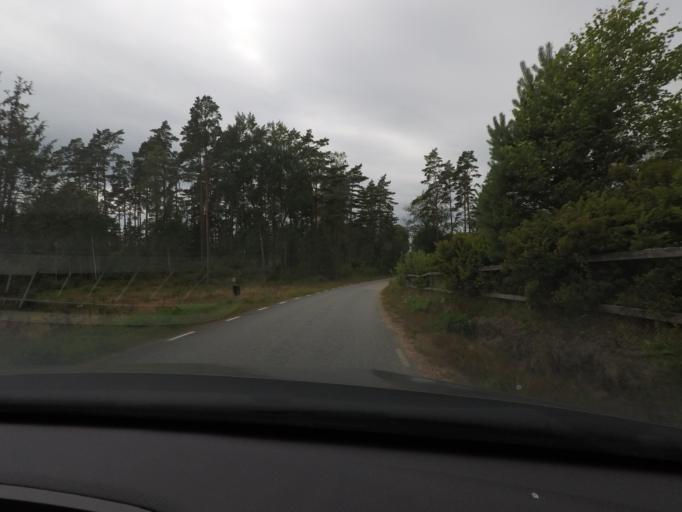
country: SE
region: Kronoberg
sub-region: Markaryds Kommun
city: Stromsnasbruk
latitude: 56.4246
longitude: 13.7630
